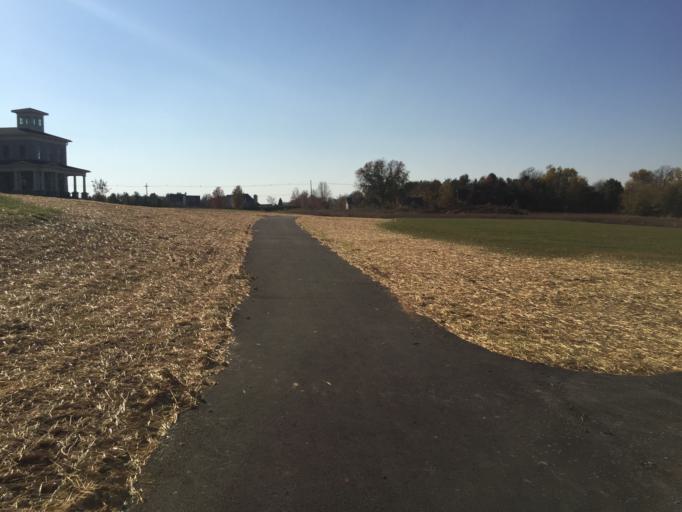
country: US
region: Kentucky
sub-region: Jefferson County
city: Worthington
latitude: 38.3292
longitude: -85.5713
